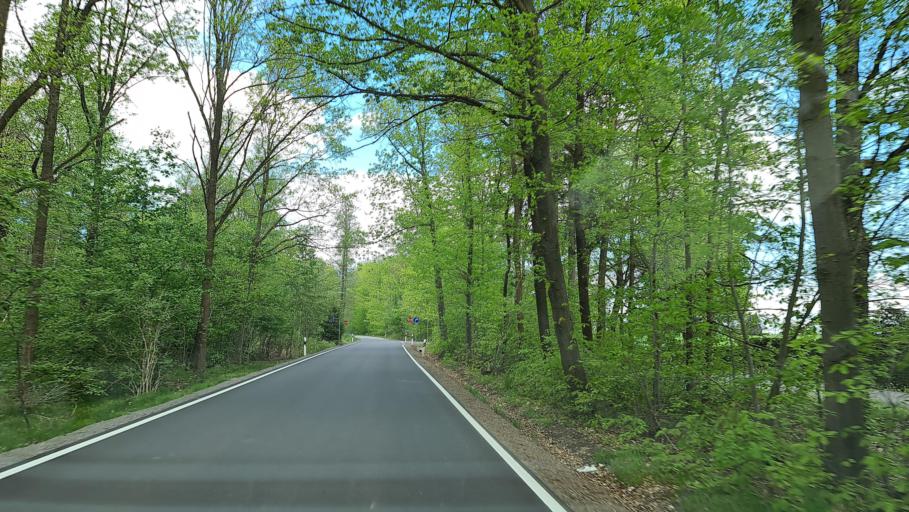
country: DE
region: Saxony
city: Hilbersdorf
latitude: 50.8394
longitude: 12.9889
